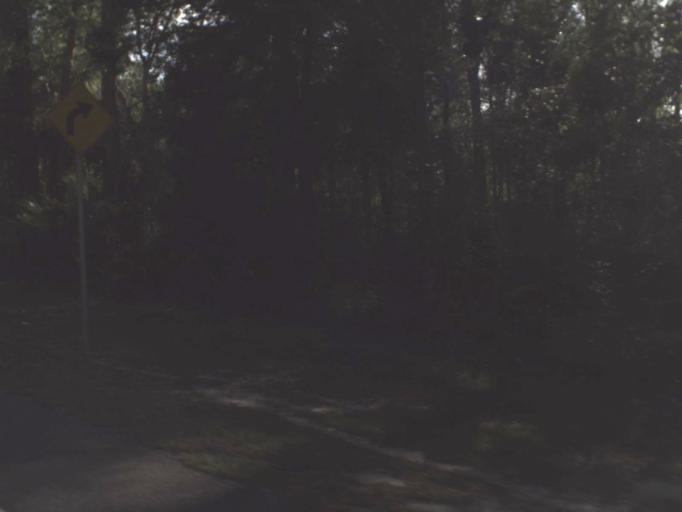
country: US
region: Florida
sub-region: Flagler County
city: Bunnell
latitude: 29.4365
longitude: -81.2832
